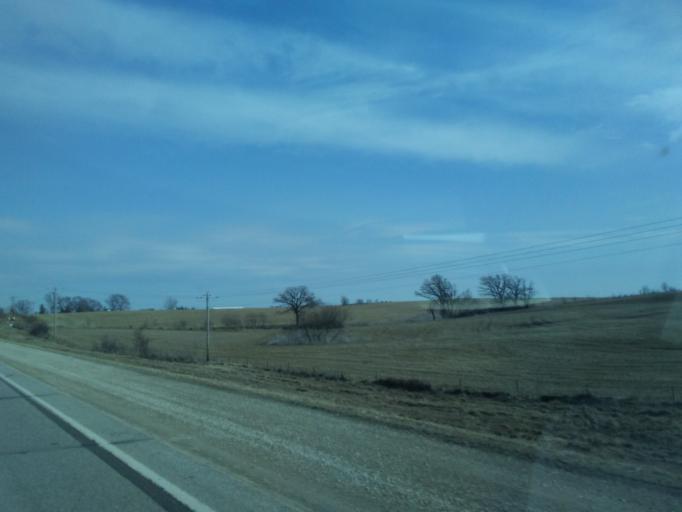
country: US
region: Iowa
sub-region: Winneshiek County
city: Decorah
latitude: 43.2409
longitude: -91.6565
